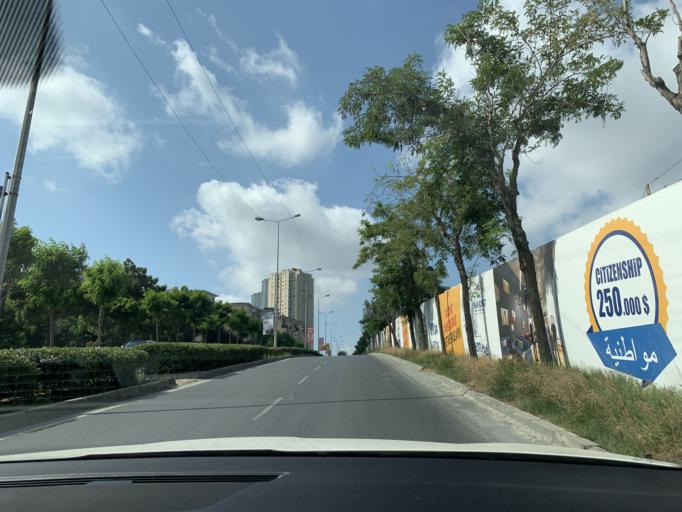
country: TR
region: Istanbul
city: Esenyurt
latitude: 41.0678
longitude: 28.7004
